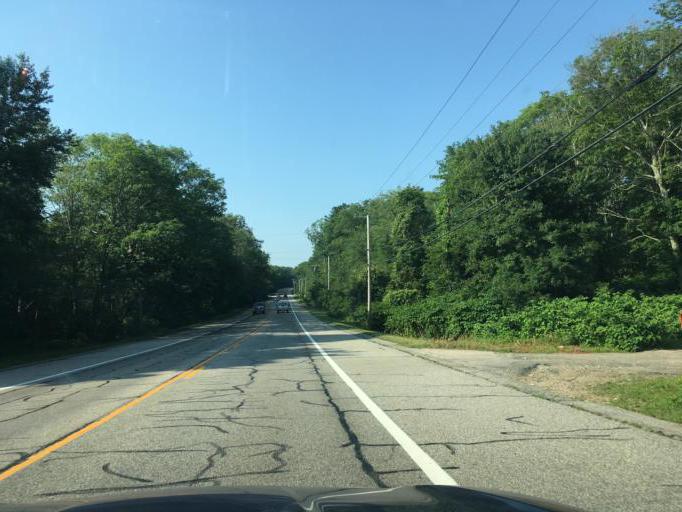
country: US
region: Rhode Island
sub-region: Washington County
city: Kingston
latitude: 41.5153
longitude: -71.5558
